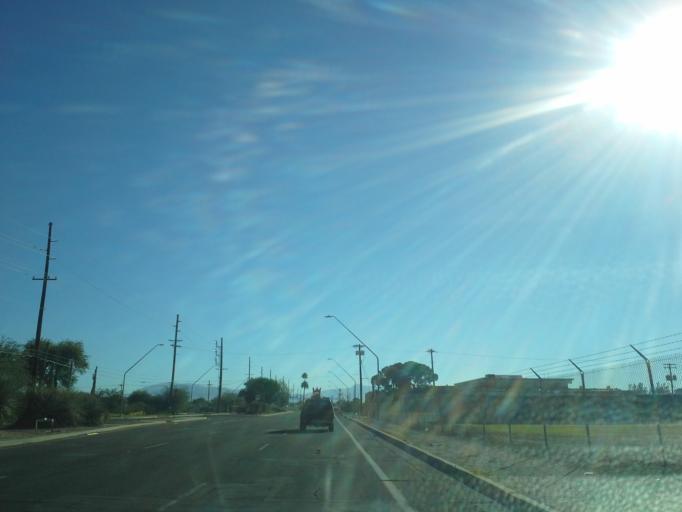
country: US
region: Arizona
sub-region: Pima County
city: Drexel Heights
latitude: 32.1339
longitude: -110.9667
